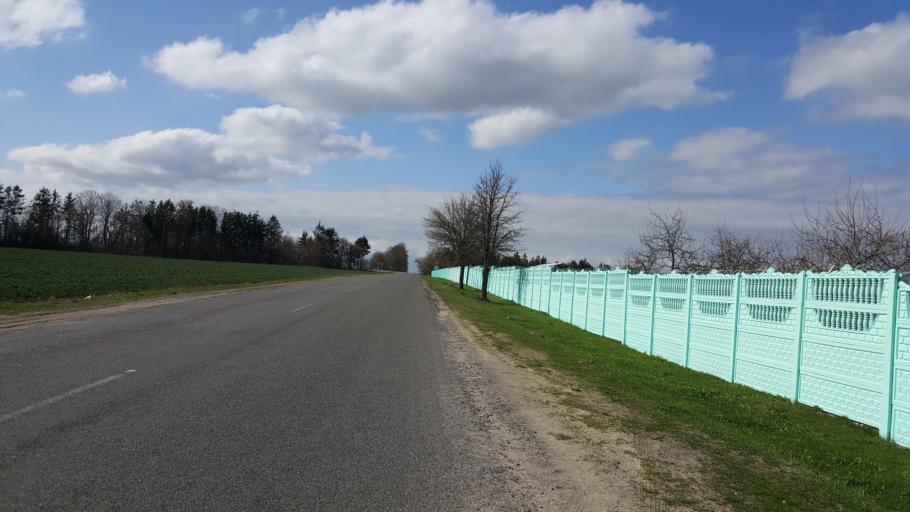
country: BY
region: Brest
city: Kamyanyets
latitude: 52.4101
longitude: 23.7921
